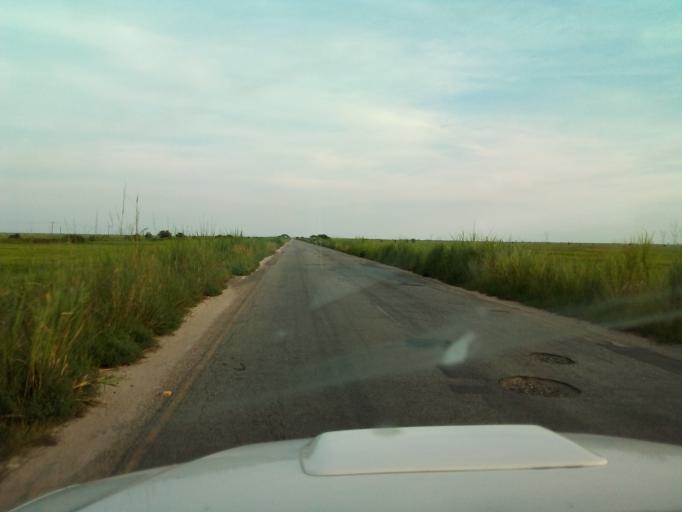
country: MZ
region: Zambezia
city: Quelimane
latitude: -17.6328
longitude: 36.8386
